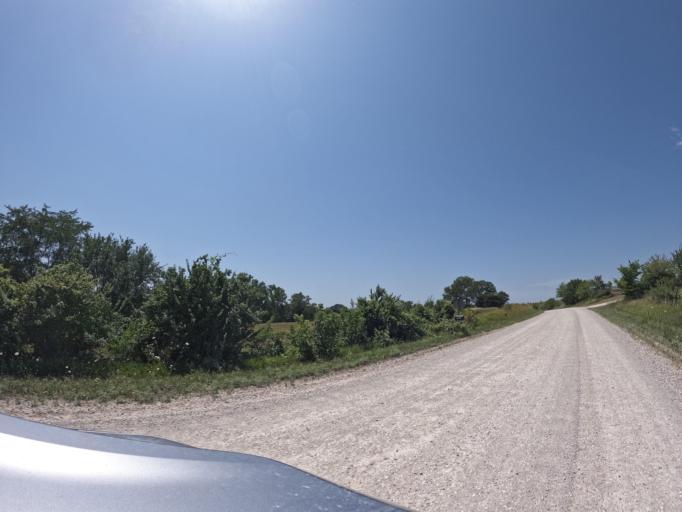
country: US
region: Iowa
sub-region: Henry County
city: Mount Pleasant
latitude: 40.9374
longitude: -91.6264
